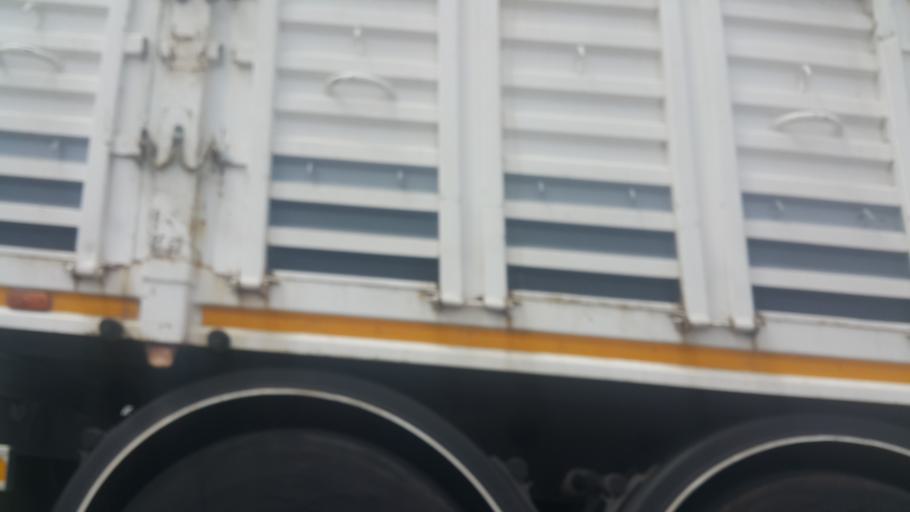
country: TR
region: Adana
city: Ceyhan
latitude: 37.0459
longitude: 35.7659
